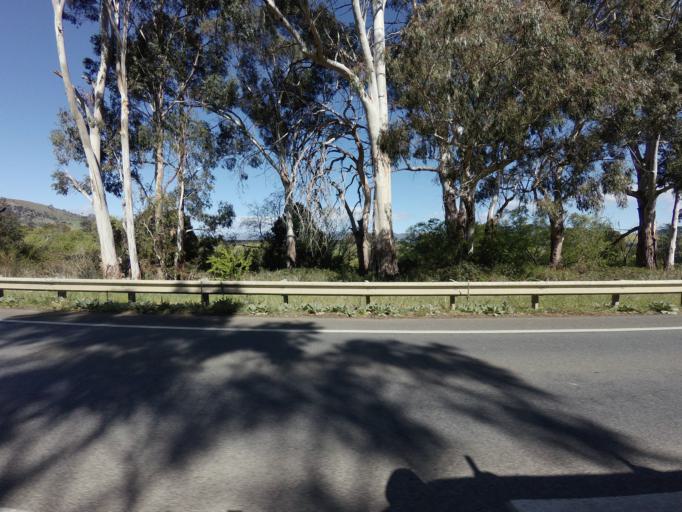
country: AU
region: Tasmania
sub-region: Derwent Valley
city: New Norfolk
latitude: -42.7333
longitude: 146.9671
